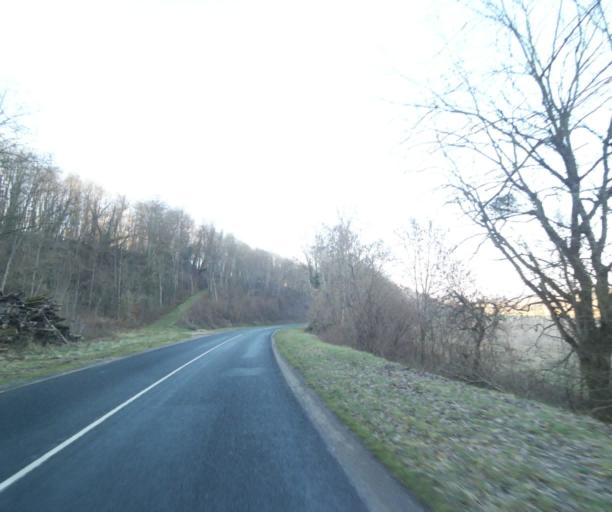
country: FR
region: Champagne-Ardenne
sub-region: Departement de la Haute-Marne
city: Bienville
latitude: 48.5700
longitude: 5.0379
